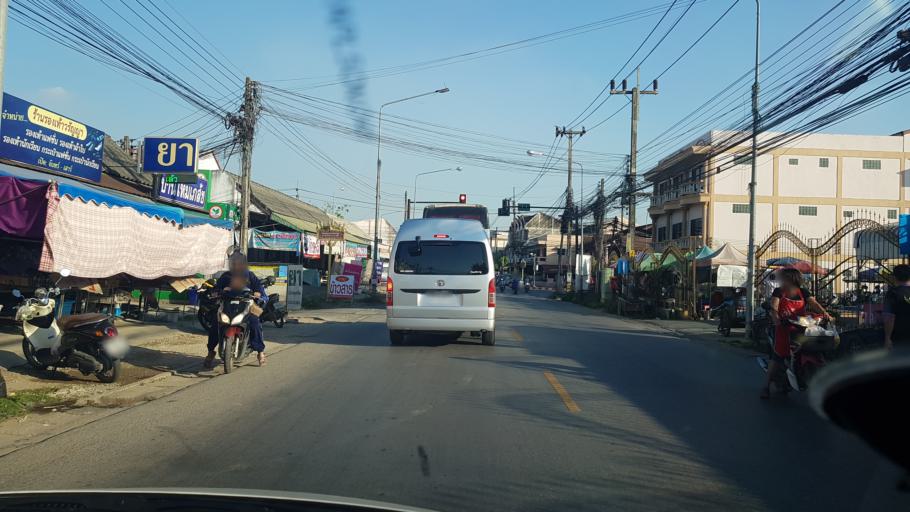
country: TH
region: Chiang Rai
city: Chiang Rai
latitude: 19.9265
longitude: 99.8360
